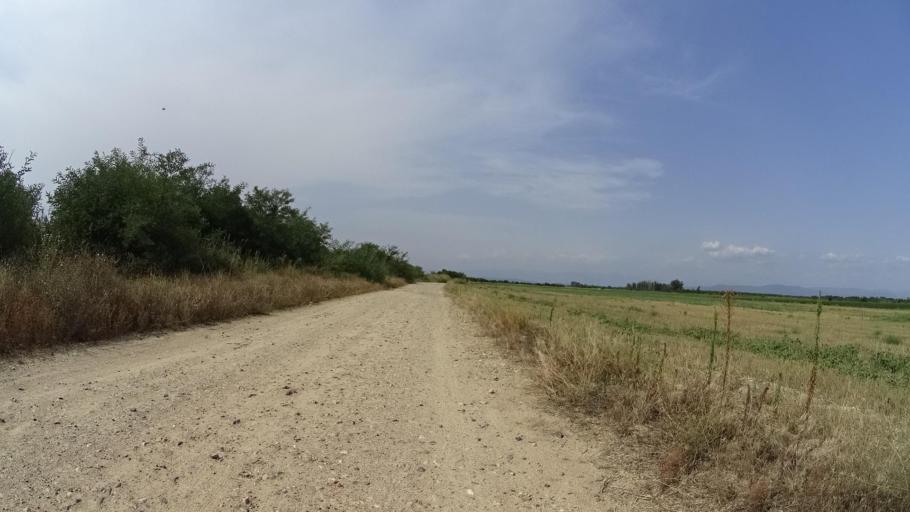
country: BG
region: Plovdiv
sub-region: Obshtina Kaloyanovo
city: Kaloyanovo
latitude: 42.2894
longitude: 24.7966
